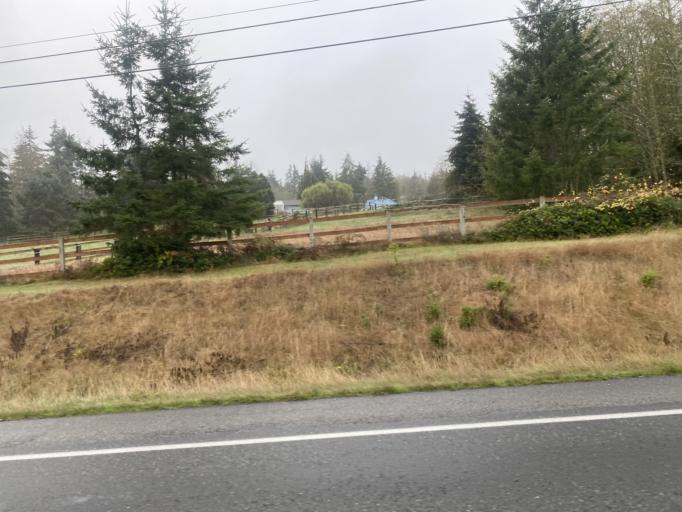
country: US
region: Washington
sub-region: Island County
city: Freeland
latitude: 48.0754
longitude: -122.5680
